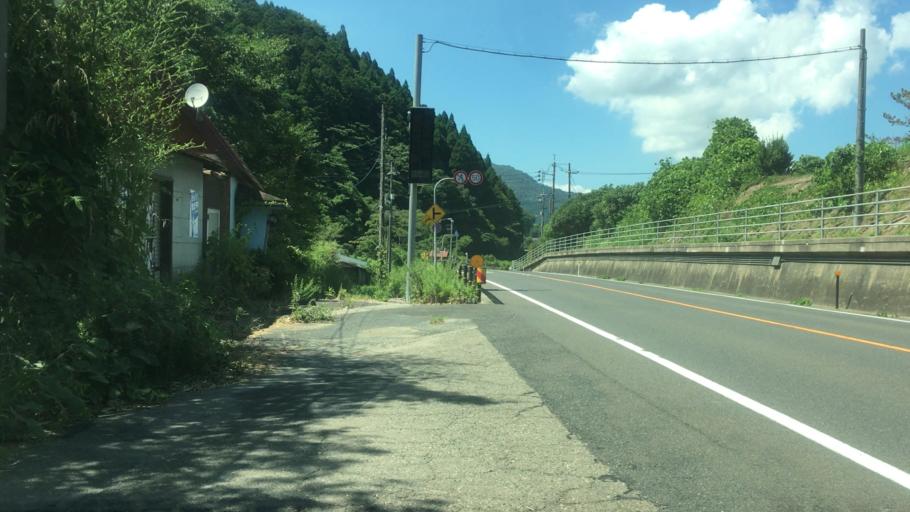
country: JP
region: Tottori
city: Tottori
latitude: 35.2446
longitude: 134.2291
